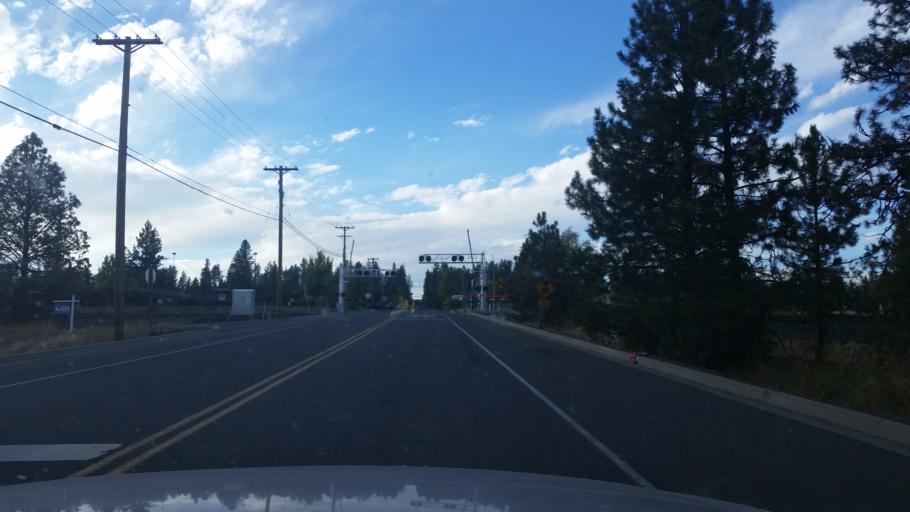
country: US
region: Washington
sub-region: Spokane County
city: Cheney
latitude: 47.4815
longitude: -117.5805
